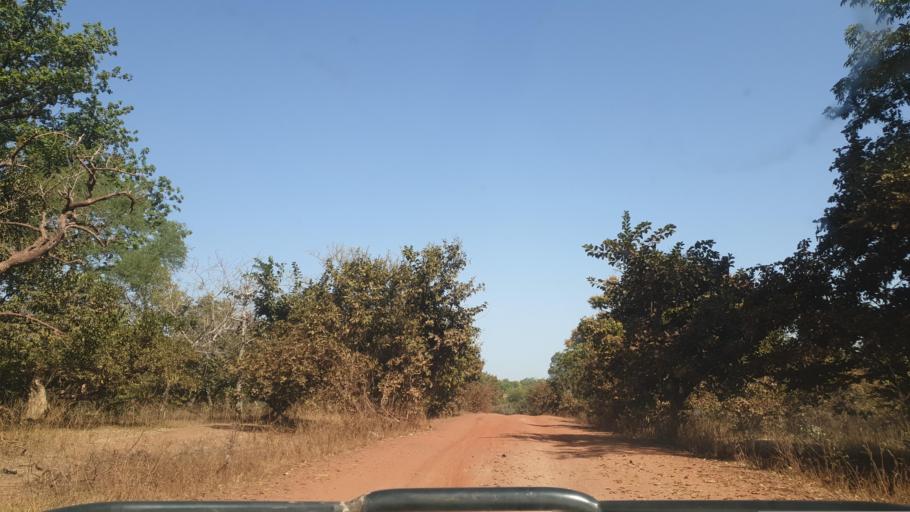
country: ML
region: Koulikoro
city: Dioila
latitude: 11.8923
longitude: -6.9807
